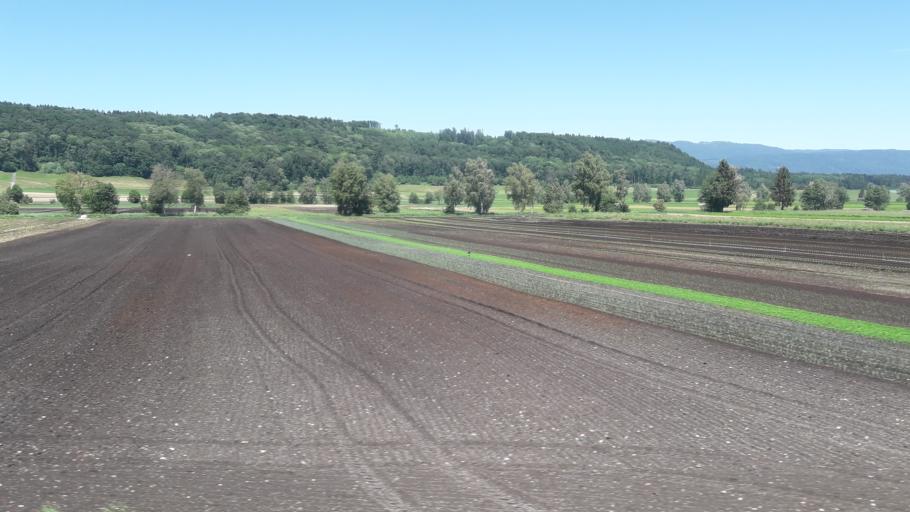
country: CH
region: Bern
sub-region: Seeland District
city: Tauffelen
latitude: 47.0275
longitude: 7.1700
